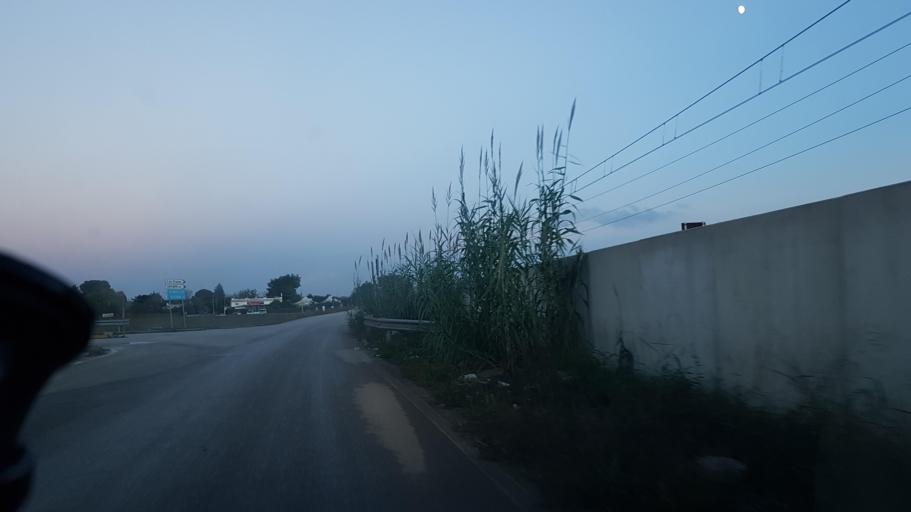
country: IT
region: Apulia
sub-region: Provincia di Brindisi
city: Latiano
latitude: 40.5590
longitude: 17.7264
